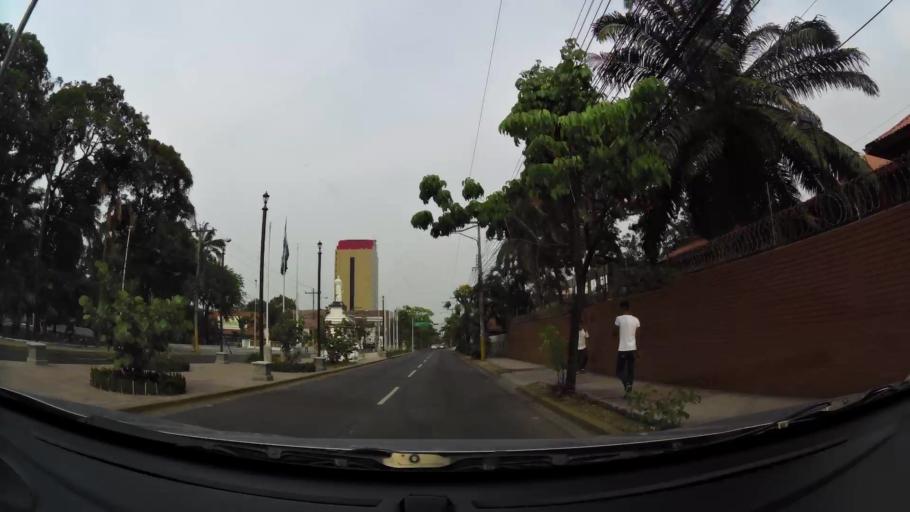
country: HN
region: Cortes
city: San Pedro Sula
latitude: 15.5065
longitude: -88.0330
